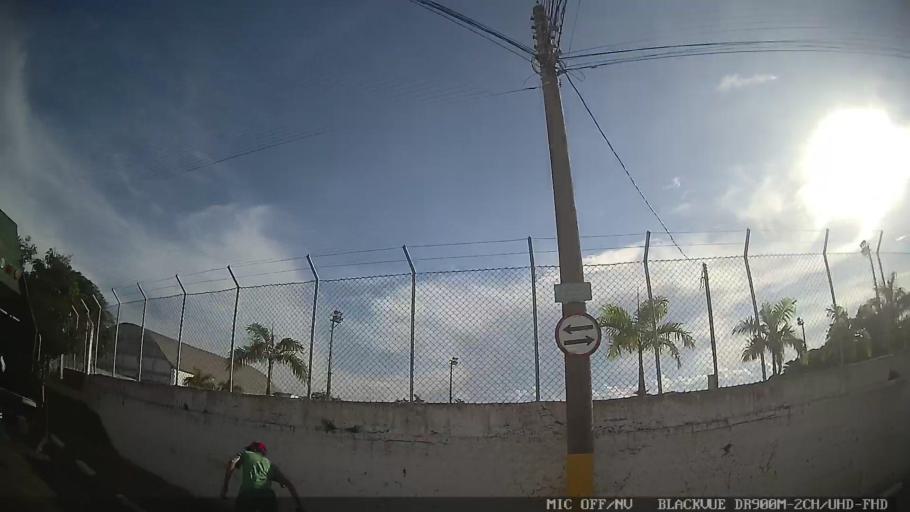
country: BR
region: Sao Paulo
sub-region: Tiete
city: Tiete
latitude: -23.1109
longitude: -47.7162
